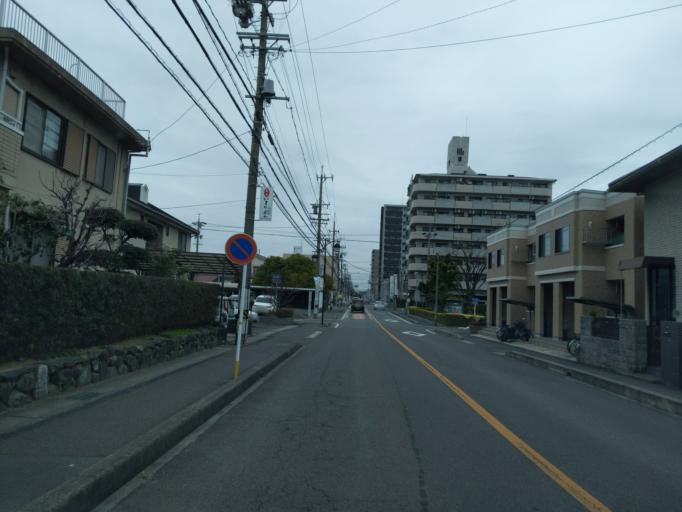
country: JP
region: Aichi
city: Kasugai
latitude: 35.2433
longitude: 136.9732
